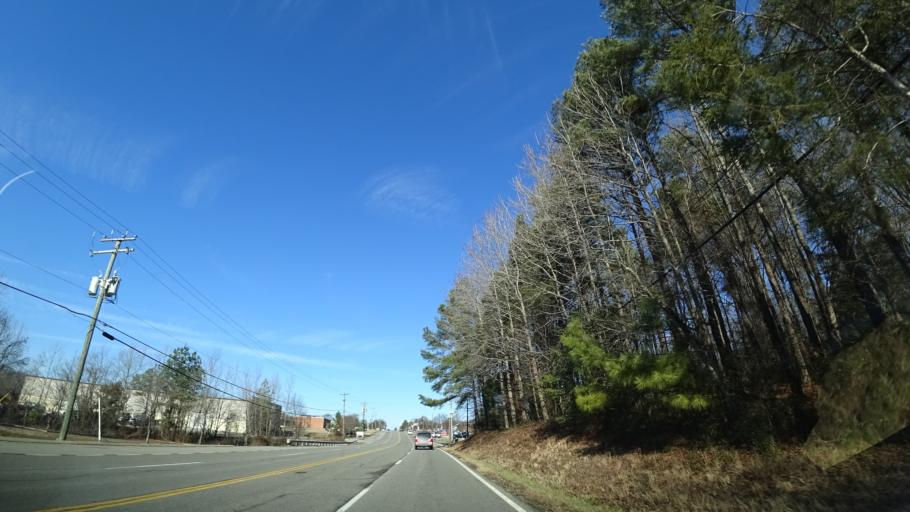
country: US
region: Virginia
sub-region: Henrico County
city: Glen Allen
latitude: 37.6971
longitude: -77.4635
